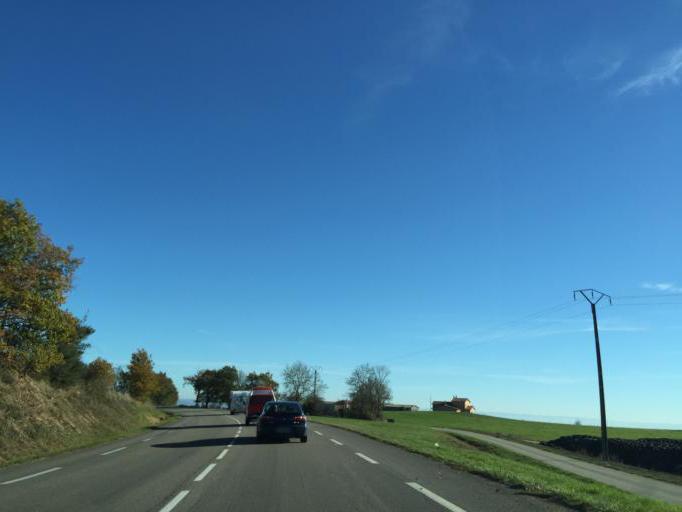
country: FR
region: Rhone-Alpes
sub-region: Departement de la Loire
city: Saint-Germain-Laval
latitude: 45.9076
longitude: 3.9988
